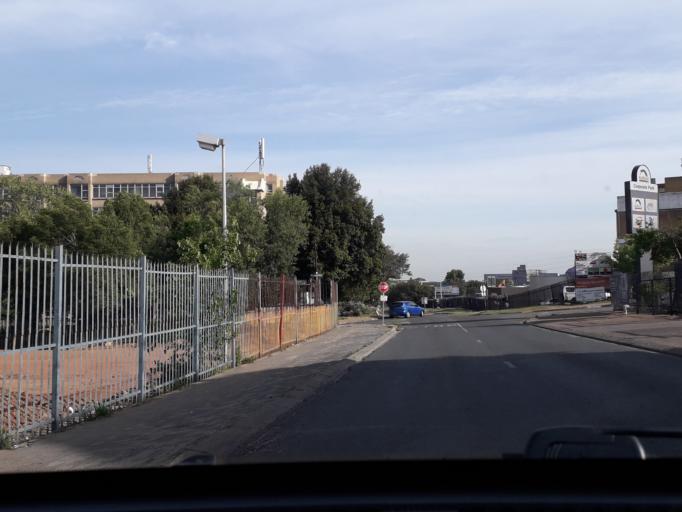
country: ZA
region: Gauteng
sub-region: City of Johannesburg Metropolitan Municipality
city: Modderfontein
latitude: -26.1195
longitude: 28.0833
